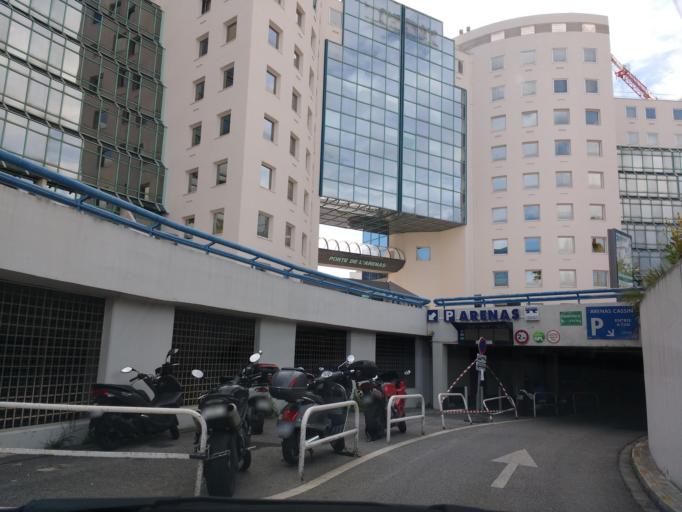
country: FR
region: Provence-Alpes-Cote d'Azur
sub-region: Departement des Alpes-Maritimes
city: Saint-Laurent-du-Var
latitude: 43.6681
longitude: 7.2149
